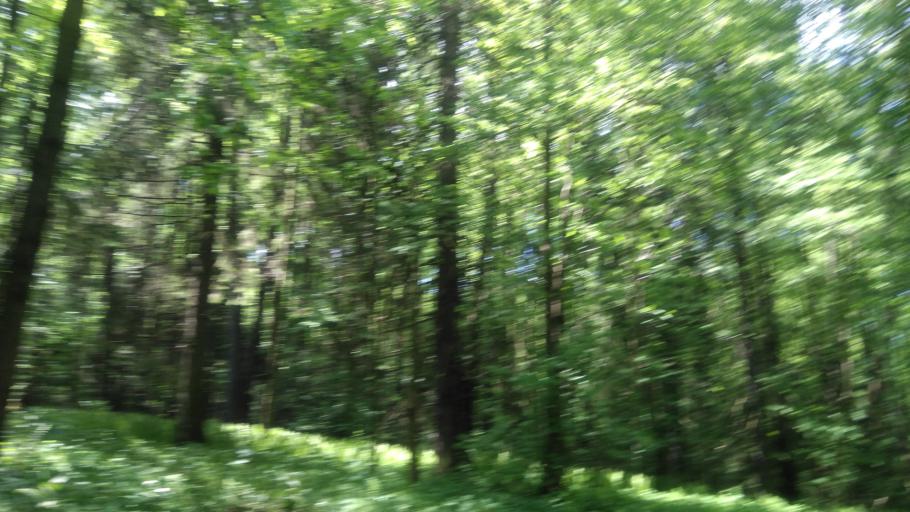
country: RU
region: Perm
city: Ferma
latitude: 57.9680
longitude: 56.3381
